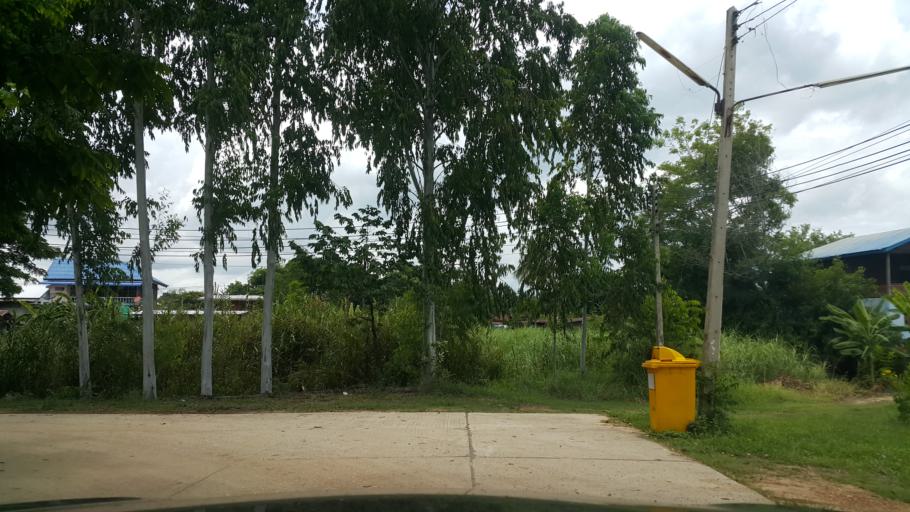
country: TH
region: Sukhothai
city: Kong Krailat
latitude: 16.9331
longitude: 99.9574
